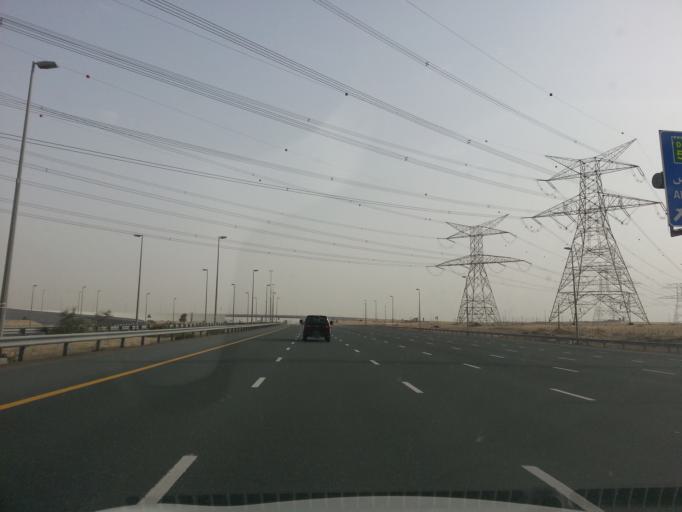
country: AE
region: Dubai
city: Dubai
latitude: 24.9840
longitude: 55.2433
